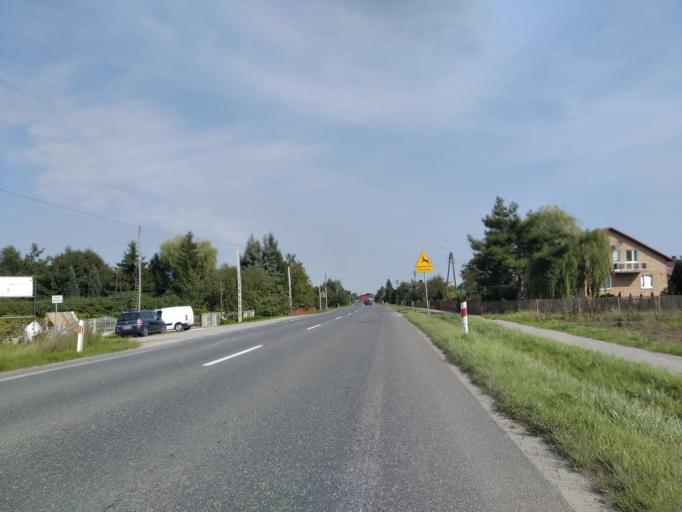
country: PL
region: Subcarpathian Voivodeship
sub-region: Powiat mielecki
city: Przeclaw
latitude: 50.1884
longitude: 21.5011
